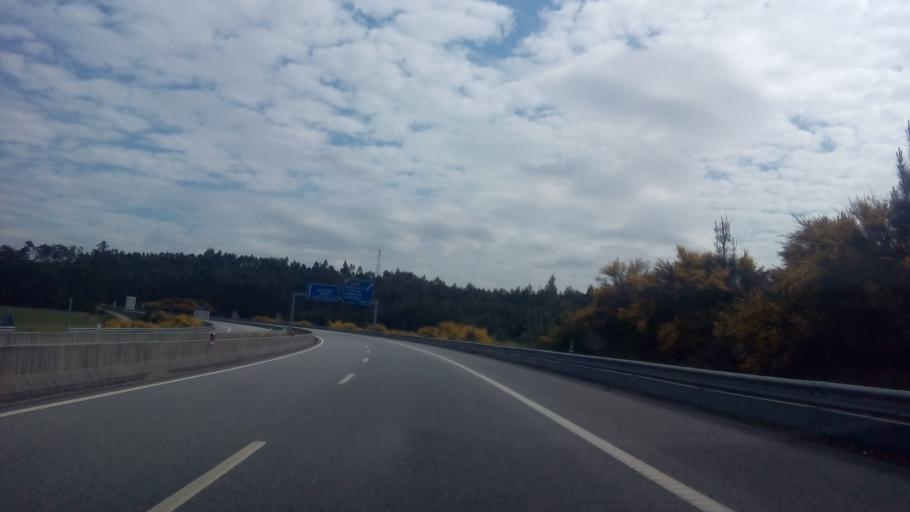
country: PT
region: Porto
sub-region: Valongo
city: Sobrado
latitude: 41.1959
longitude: -8.4517
